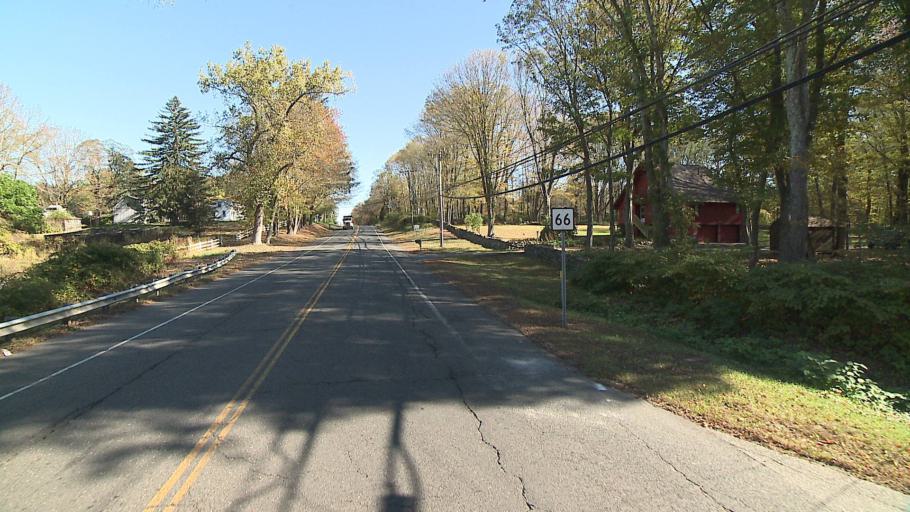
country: US
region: Connecticut
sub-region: Tolland County
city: Hebron
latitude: 41.6923
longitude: -72.3148
